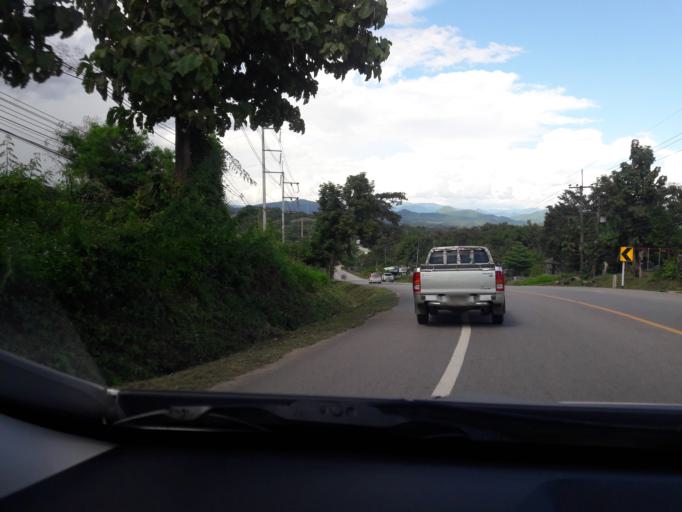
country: TH
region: Mae Hong Son
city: Mae Hi
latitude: 19.3393
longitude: 98.4335
